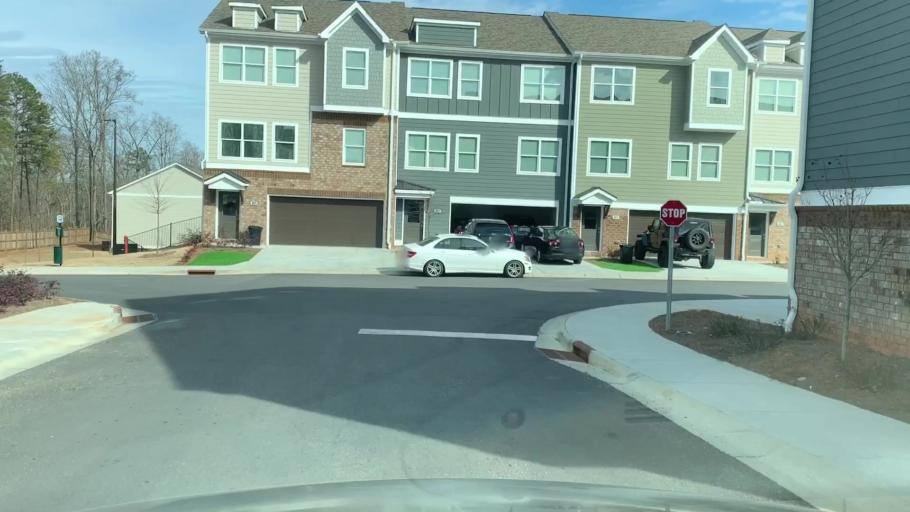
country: US
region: South Carolina
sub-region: Pickens County
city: Central
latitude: 34.6920
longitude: -82.7848
